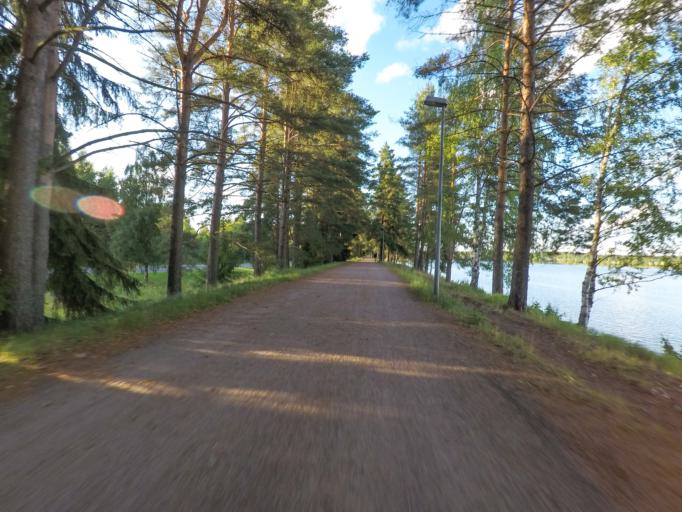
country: FI
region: South Karelia
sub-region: Imatra
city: Imatra
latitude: 61.1760
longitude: 28.7816
